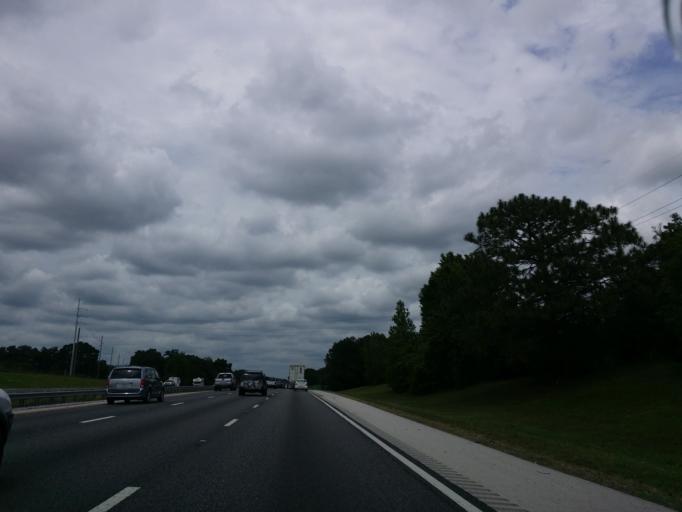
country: US
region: Florida
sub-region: Marion County
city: Ocala
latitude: 29.2781
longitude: -82.1969
